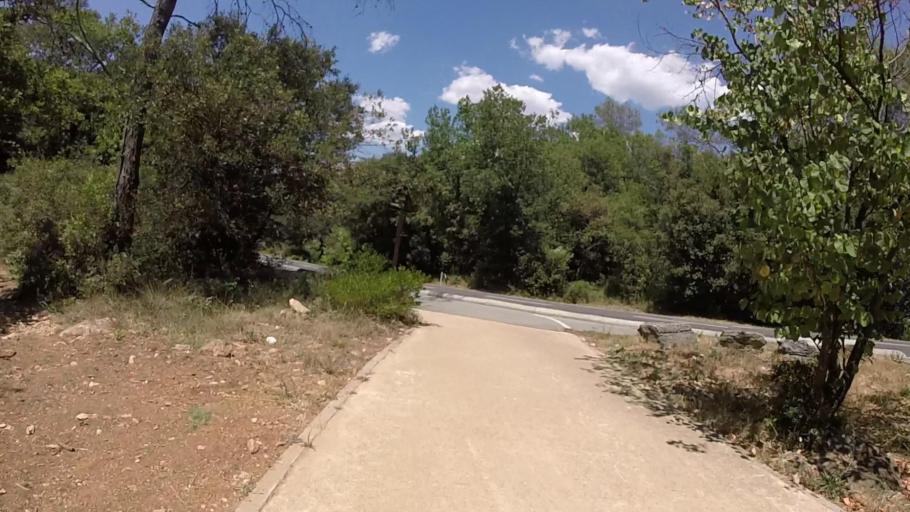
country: FR
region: Provence-Alpes-Cote d'Azur
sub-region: Departement des Alpes-Maritimes
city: Vallauris
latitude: 43.6134
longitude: 7.0442
